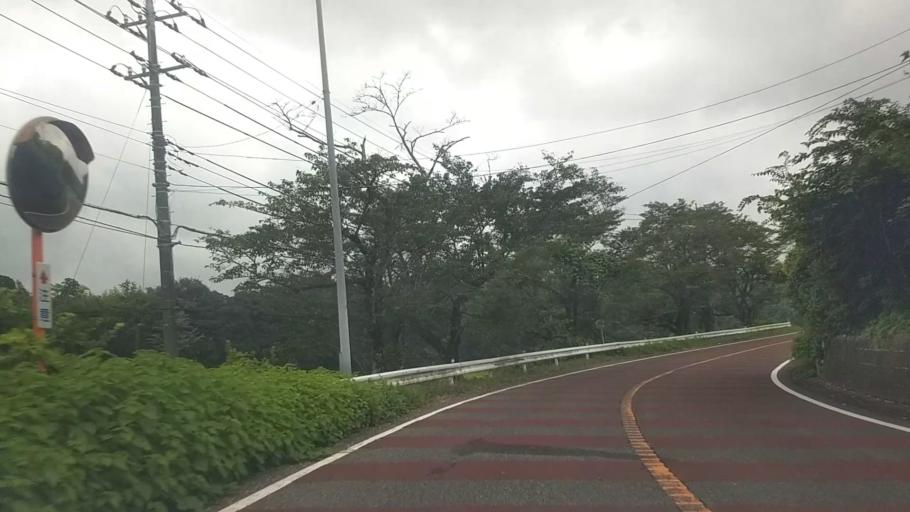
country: JP
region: Chiba
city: Kawaguchi
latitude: 35.2399
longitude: 140.0757
